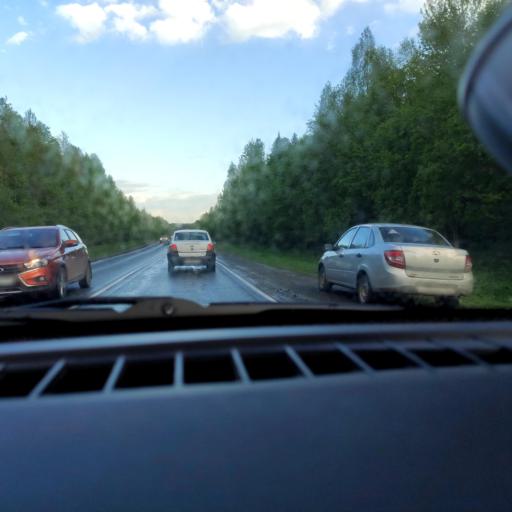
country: RU
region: Perm
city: Perm
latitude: 58.1754
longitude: 56.2301
